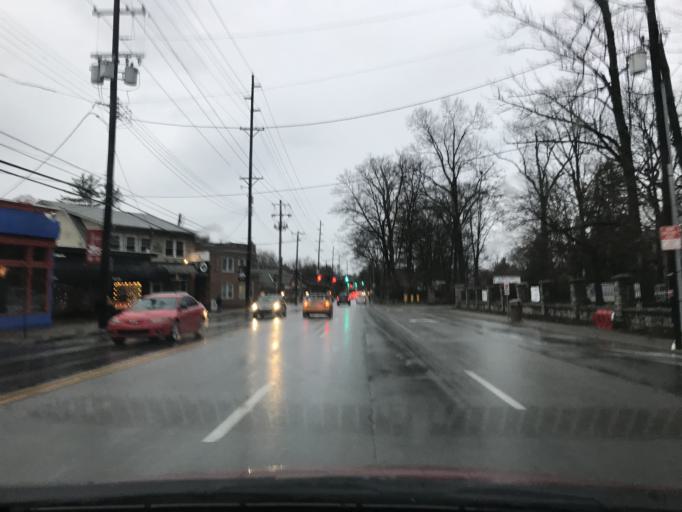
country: US
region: Kentucky
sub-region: Jefferson County
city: Audubon Park
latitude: 38.2249
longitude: -85.6944
